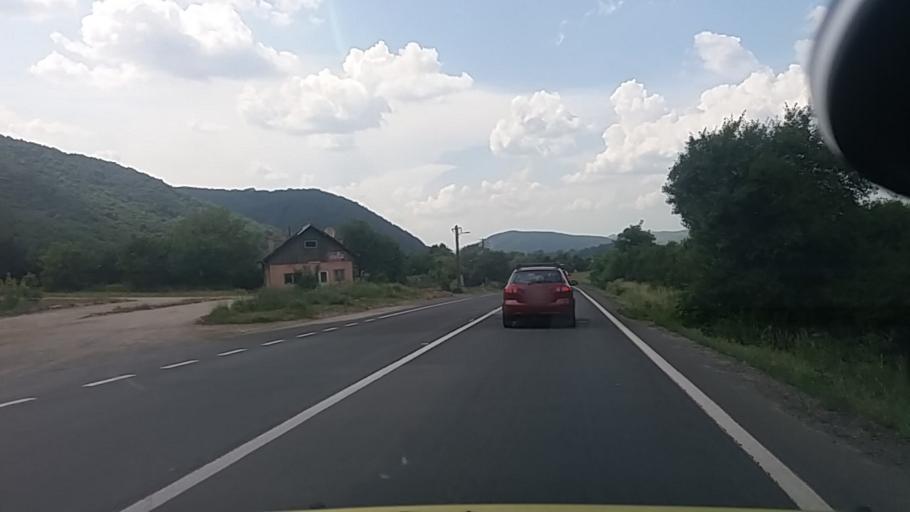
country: RO
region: Hunedoara
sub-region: Comuna Branisca
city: Branisca
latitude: 45.9043
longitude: 22.7865
